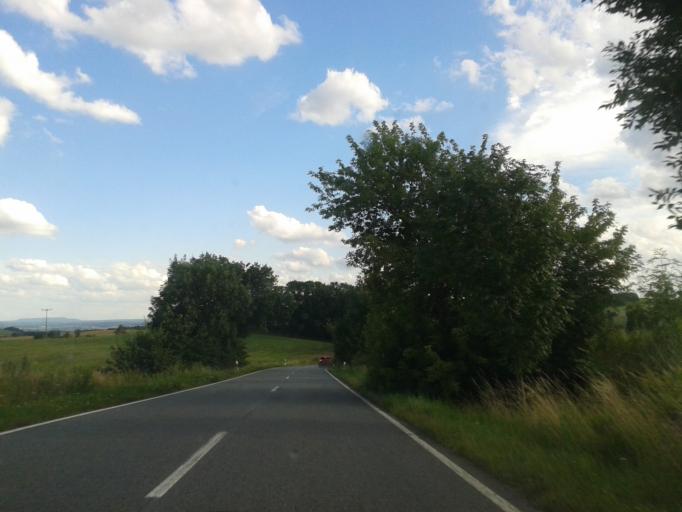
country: DE
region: Saxony
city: Durrrohrsdorf
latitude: 51.0492
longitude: 13.9362
